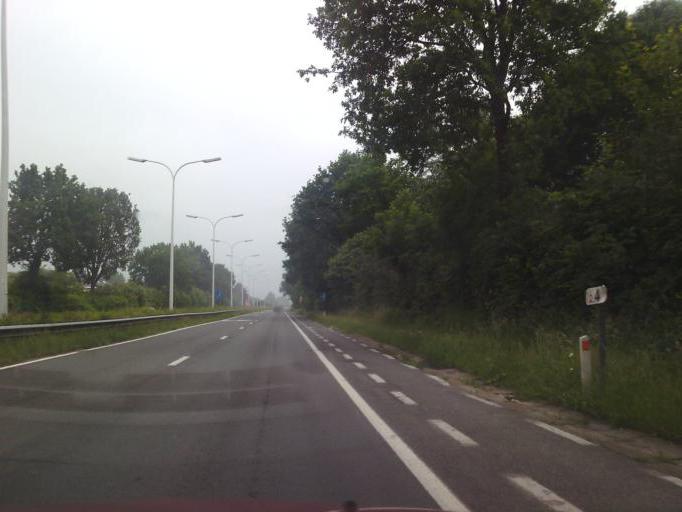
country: BE
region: Flanders
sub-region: Provincie Oost-Vlaanderen
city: Aalst
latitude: 50.9664
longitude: 4.0394
